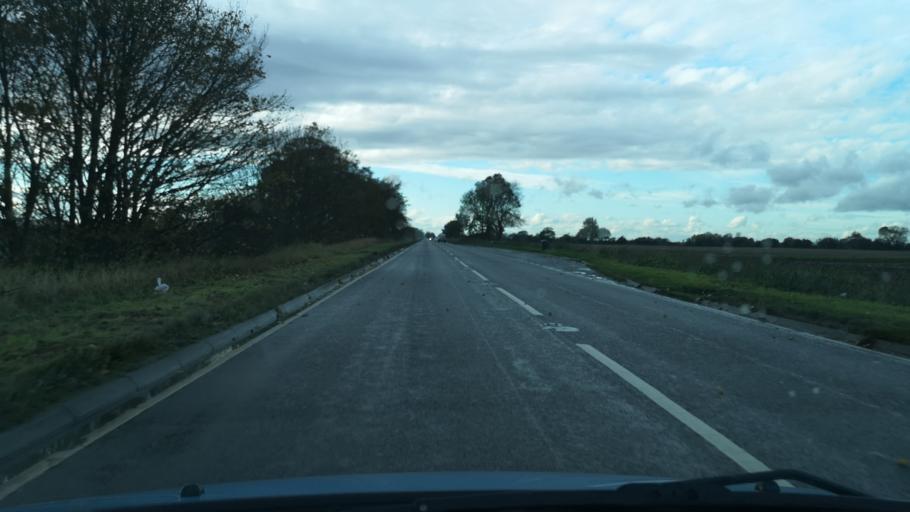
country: GB
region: England
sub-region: North Lincolnshire
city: Crowle
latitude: 53.5810
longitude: -0.8873
